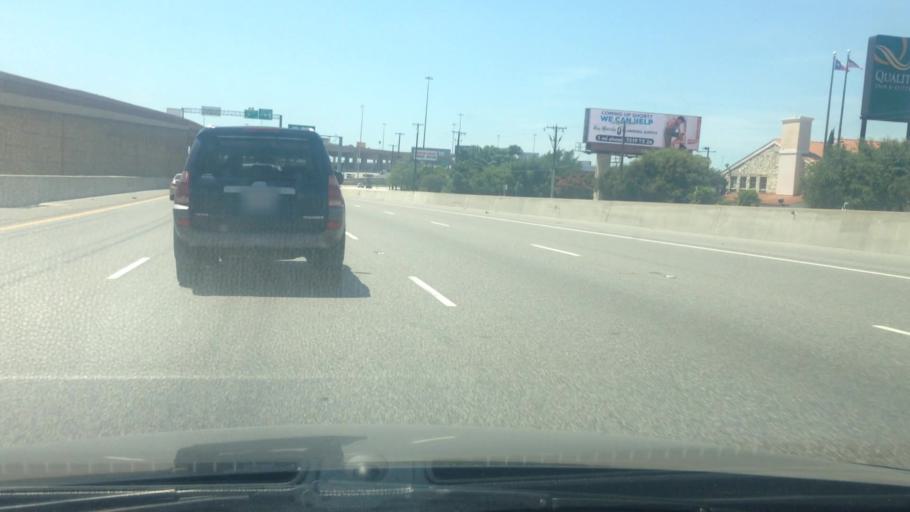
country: US
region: Texas
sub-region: Tarrant County
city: Hurst
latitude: 32.8374
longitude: -97.1965
